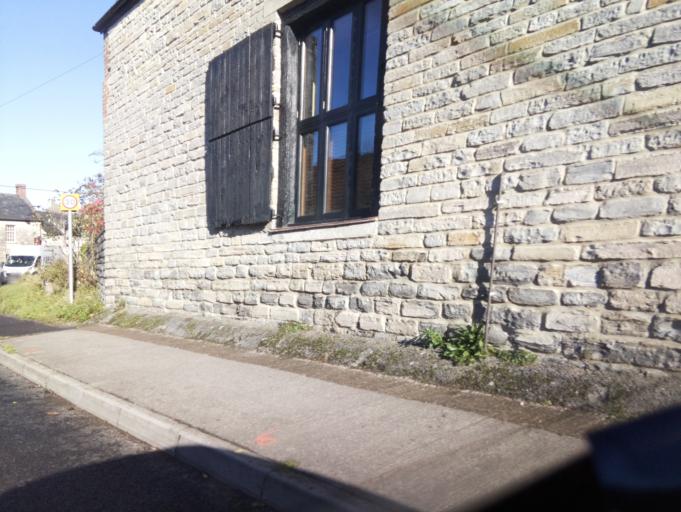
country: GB
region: England
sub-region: Somerset
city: Langport
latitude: 51.0591
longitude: -2.8569
